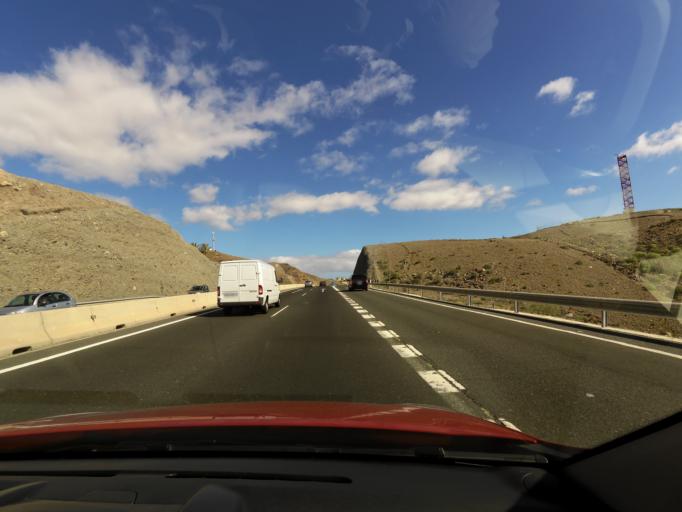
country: ES
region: Canary Islands
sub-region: Provincia de Las Palmas
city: Maspalomas
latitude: 27.7701
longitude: -15.6437
